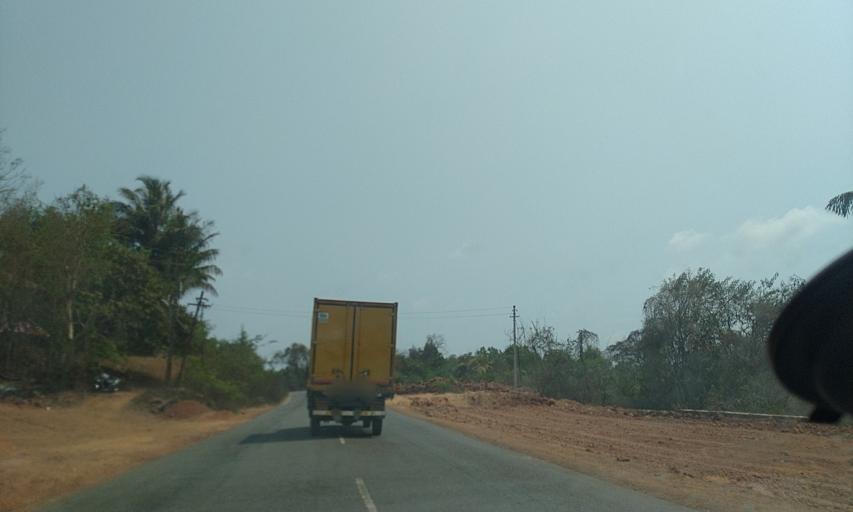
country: IN
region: Goa
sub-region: North Goa
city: Pernem
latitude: 15.6895
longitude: 73.8286
